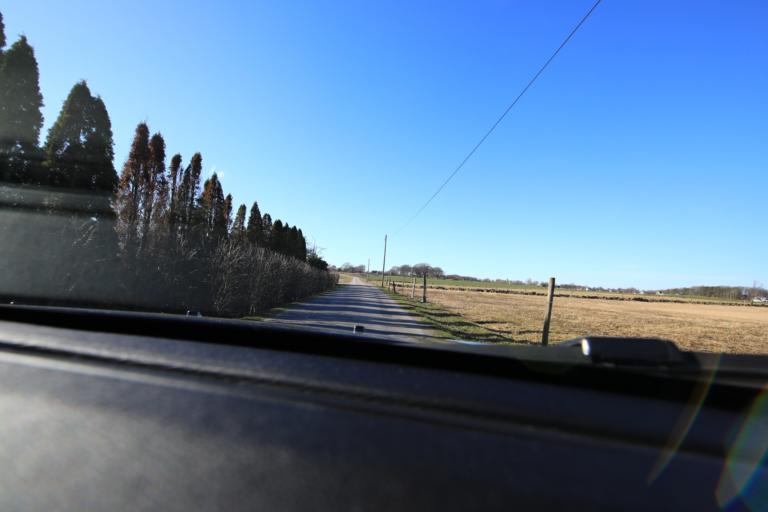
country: SE
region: Halland
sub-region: Varbergs Kommun
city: Tvaaker
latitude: 57.0658
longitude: 12.3874
